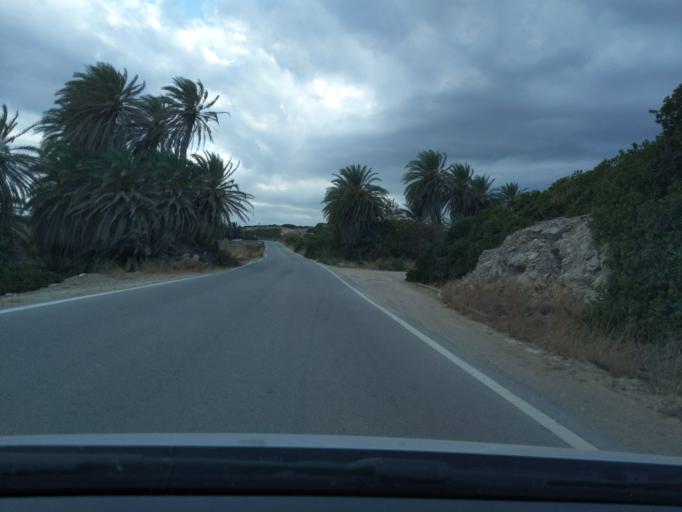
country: GR
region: Crete
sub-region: Nomos Lasithiou
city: Palekastro
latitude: 35.2520
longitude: 26.2523
